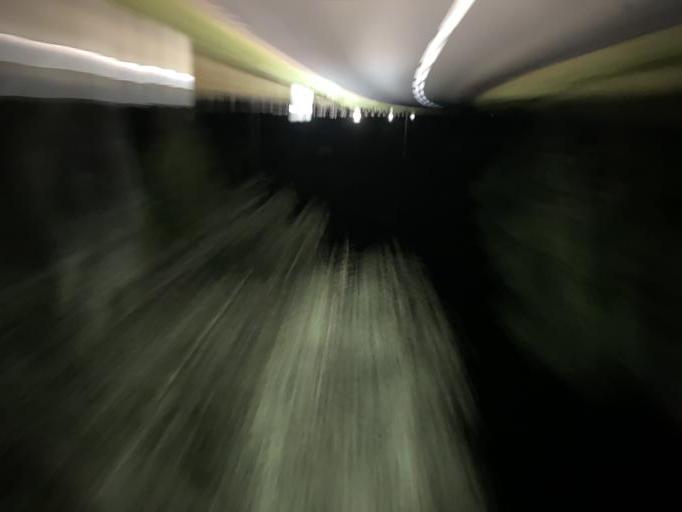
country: FR
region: Auvergne
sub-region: Departement du Puy-de-Dome
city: Lezoux
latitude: 45.8138
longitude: 3.3952
